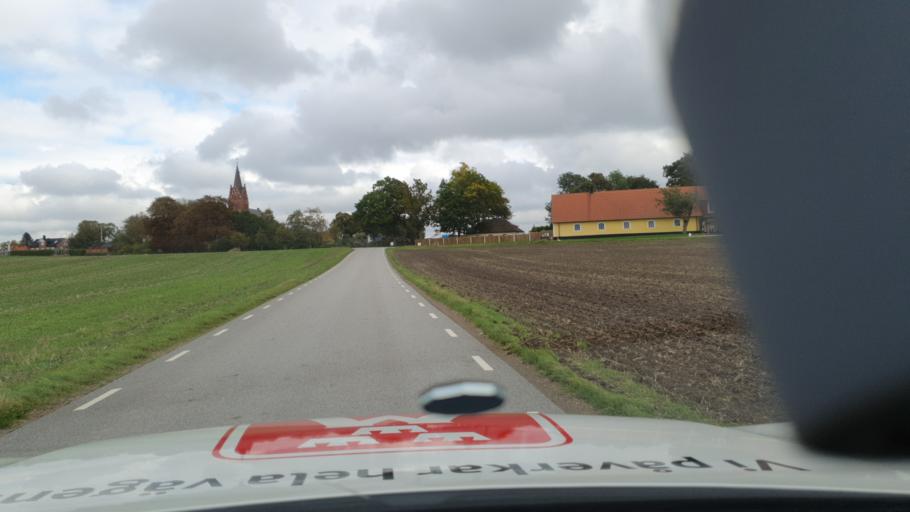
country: SE
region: Skane
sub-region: Vellinge Kommun
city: Vellinge
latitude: 55.4468
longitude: 13.0792
